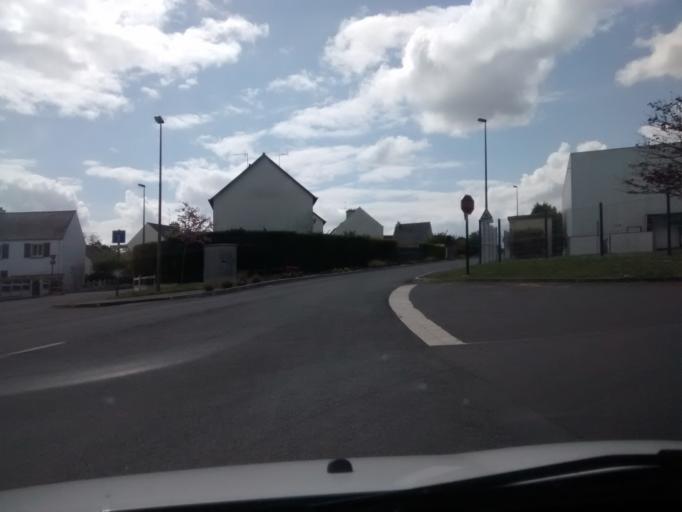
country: FR
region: Brittany
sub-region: Departement des Cotes-d'Armor
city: Lanvallay
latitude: 48.4692
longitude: -2.0435
